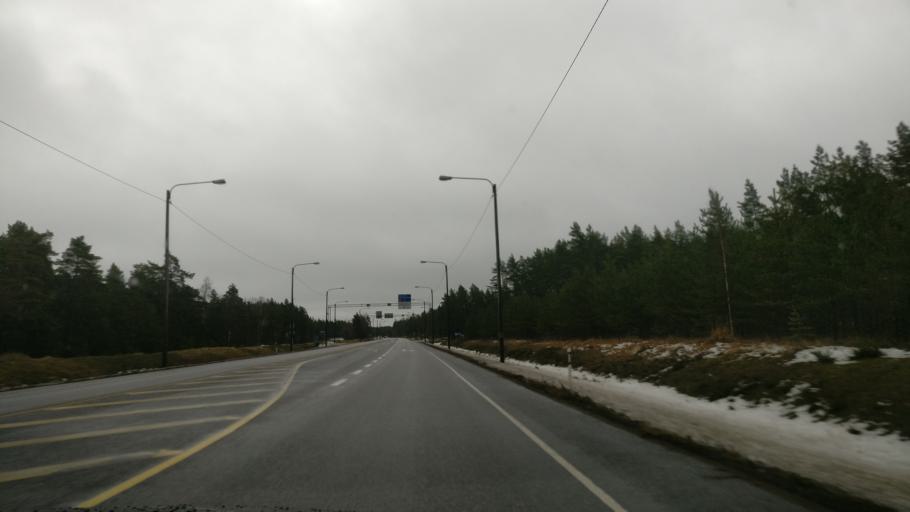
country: FI
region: Uusimaa
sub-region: Raaseporin
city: Hanko
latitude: 59.8558
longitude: 23.0195
